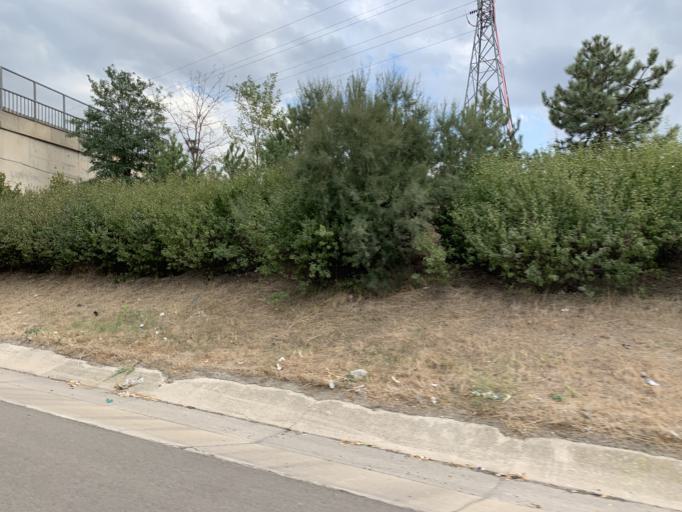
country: TR
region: Bursa
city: Gorukle
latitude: 40.2552
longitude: 28.8105
